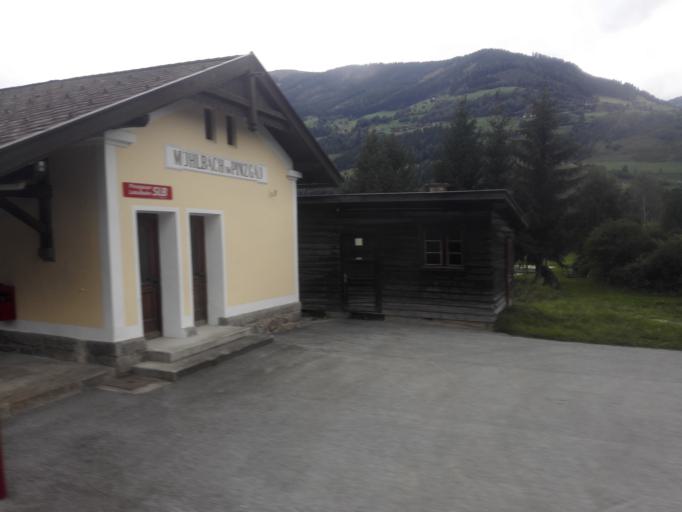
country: AT
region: Salzburg
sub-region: Politischer Bezirk Zell am See
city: Bramberg am Wildkogel
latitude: 47.2730
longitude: 12.3746
